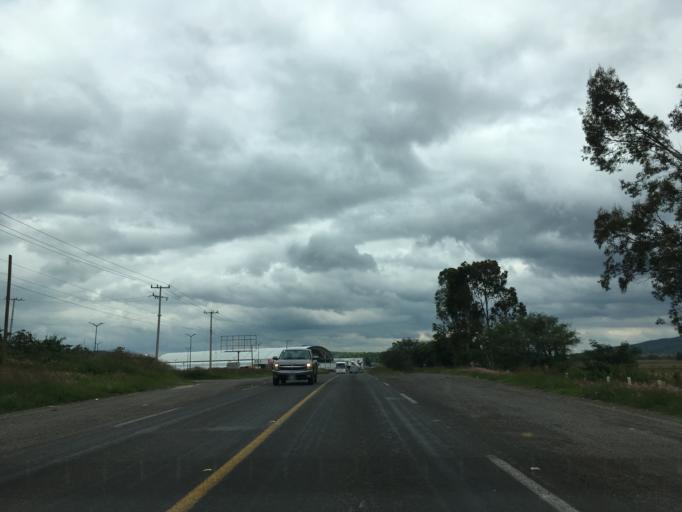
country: MX
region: Michoacan
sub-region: Cuitzeo
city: Cuamio
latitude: 20.0661
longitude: -101.1536
